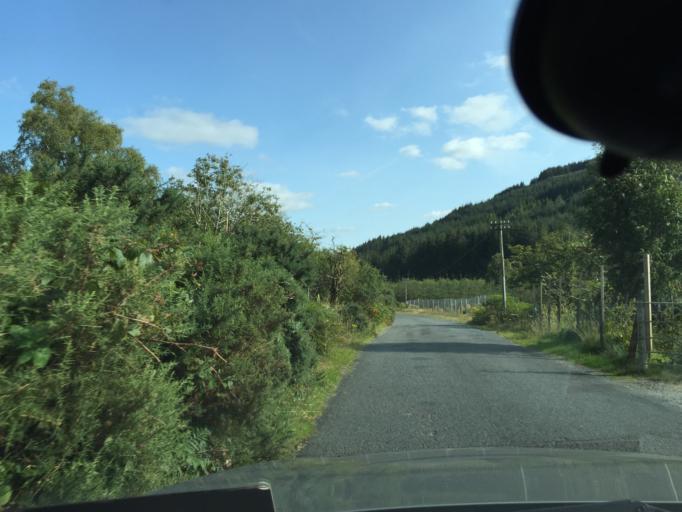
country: IE
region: Leinster
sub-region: Wicklow
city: Rathdrum
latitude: 53.0367
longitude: -6.3220
